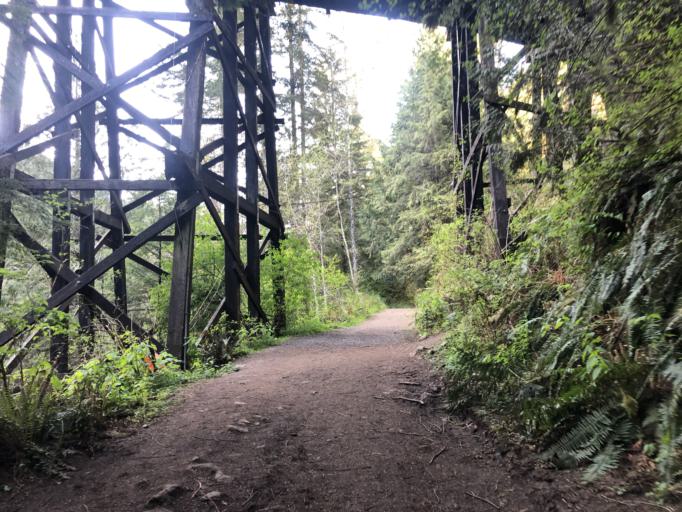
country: US
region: Washington
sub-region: Pierce County
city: Buckley
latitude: 47.0419
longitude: -122.0404
